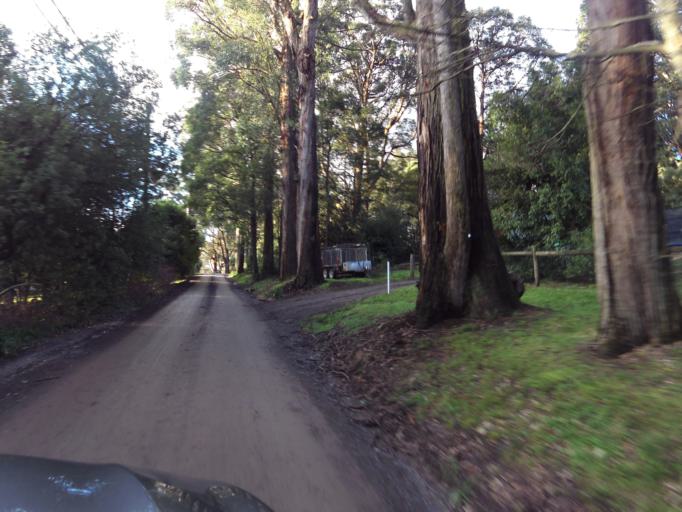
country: AU
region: Victoria
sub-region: Yarra Ranges
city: Ferny Creek
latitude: -37.8771
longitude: 145.3255
